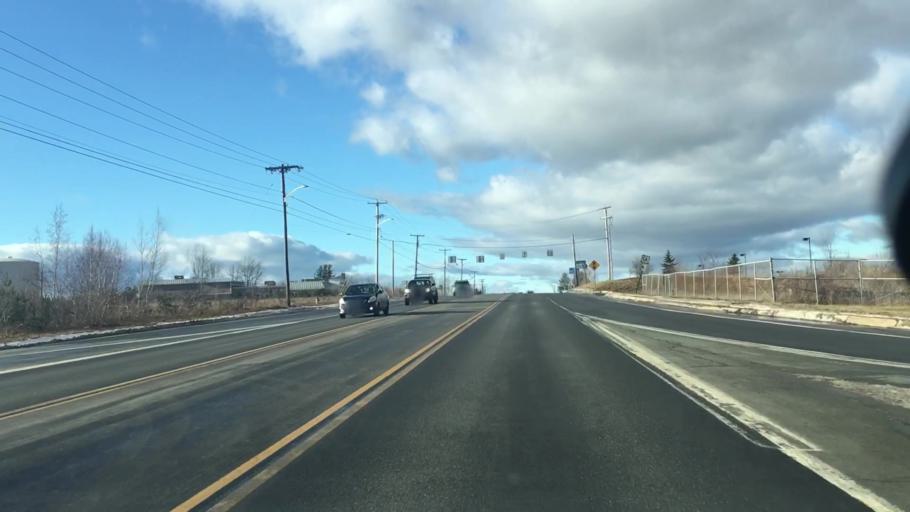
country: US
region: Maine
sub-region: Penobscot County
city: Brewer
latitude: 44.7723
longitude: -68.7238
